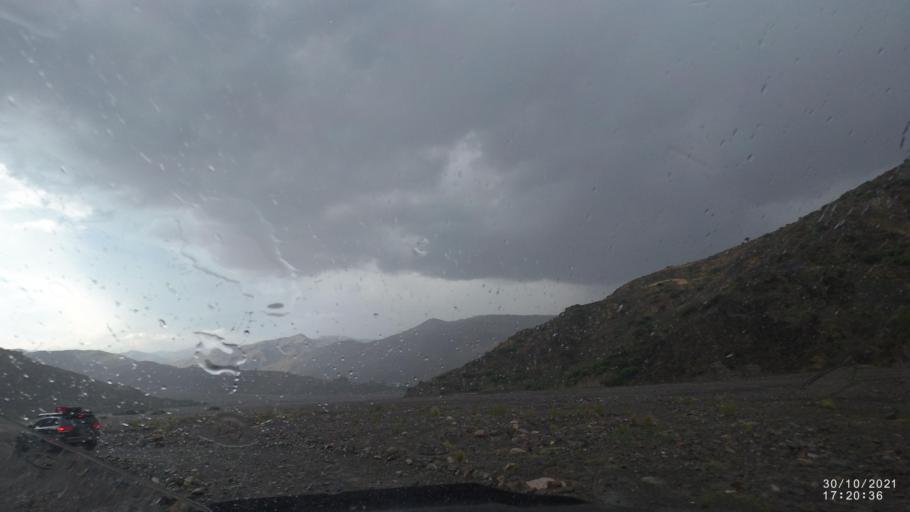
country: BO
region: Cochabamba
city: Colchani
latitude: -17.5303
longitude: -66.6189
